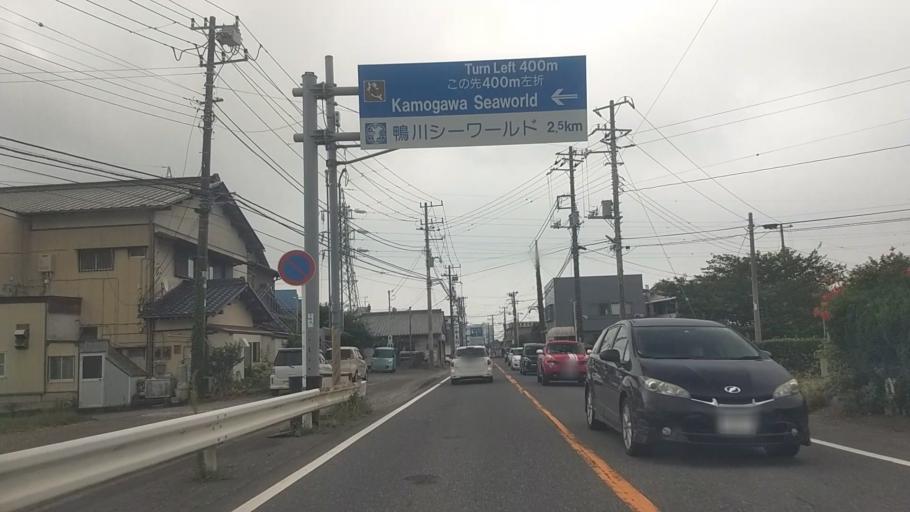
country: JP
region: Chiba
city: Kawaguchi
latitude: 35.1117
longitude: 140.0985
